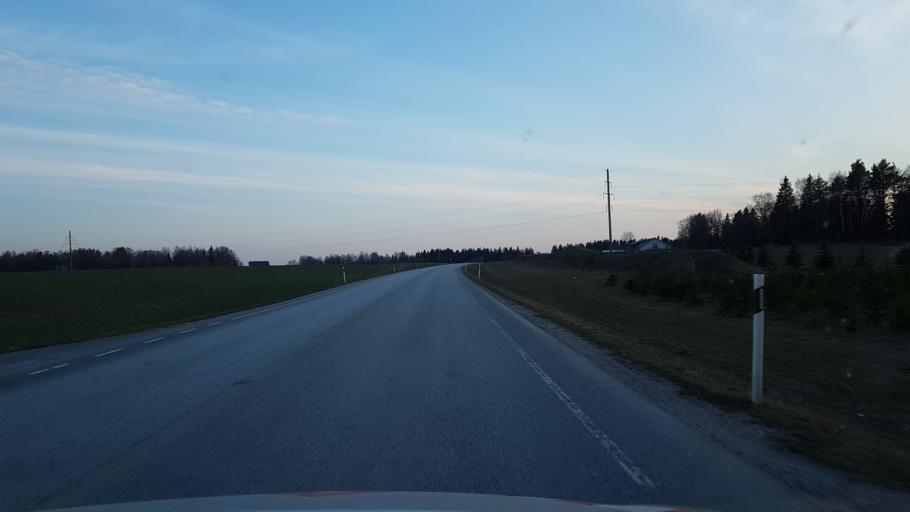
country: EE
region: Laeaene-Virumaa
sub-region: Vinni vald
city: Vinni
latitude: 59.3301
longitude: 26.4009
